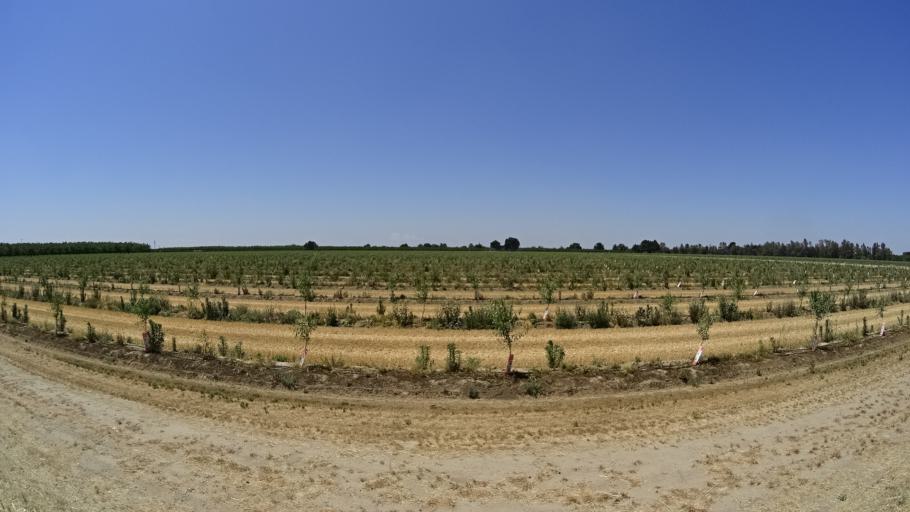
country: US
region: California
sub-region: Kings County
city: Lucerne
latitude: 36.4292
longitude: -119.6008
